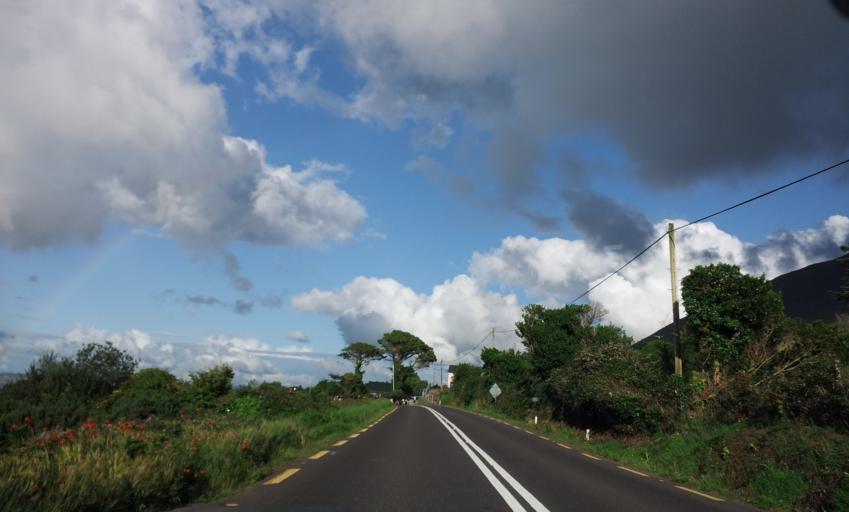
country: IE
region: Munster
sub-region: Ciarrai
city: Killorglin
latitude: 52.2269
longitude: -9.8891
